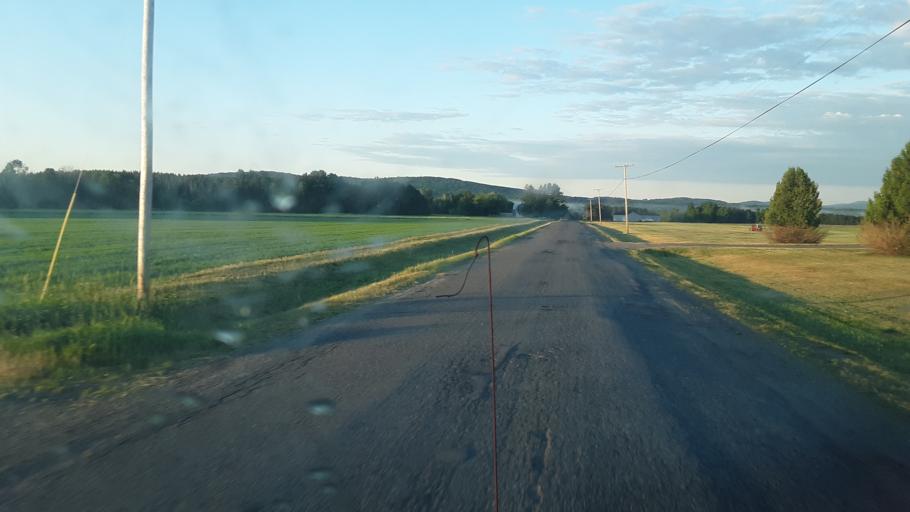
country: US
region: Maine
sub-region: Aroostook County
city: Presque Isle
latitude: 46.7700
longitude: -68.1021
